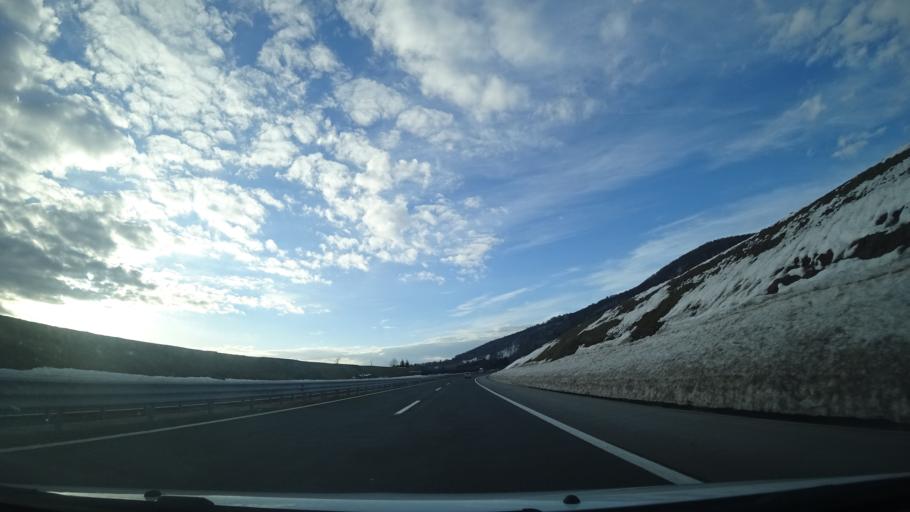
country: HR
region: Karlovacka
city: Ostarije
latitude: 45.1934
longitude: 15.2662
